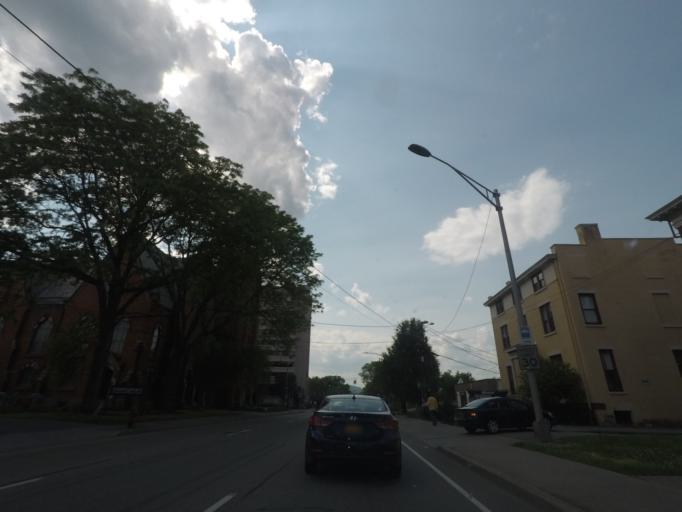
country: US
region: New York
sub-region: Dutchess County
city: Poughkeepsie
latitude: 41.7054
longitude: -73.9273
